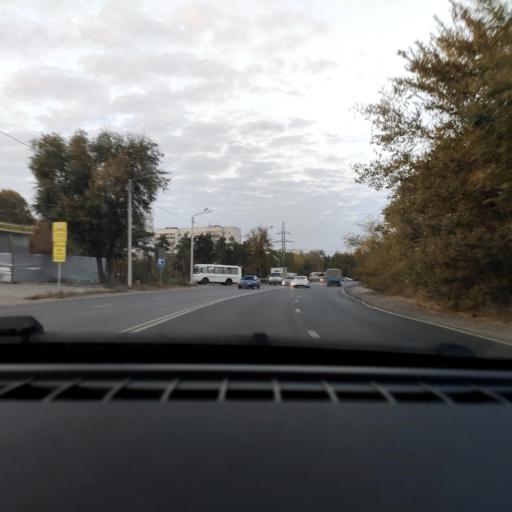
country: RU
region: Voronezj
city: Maslovka
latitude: 51.6302
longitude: 39.2867
